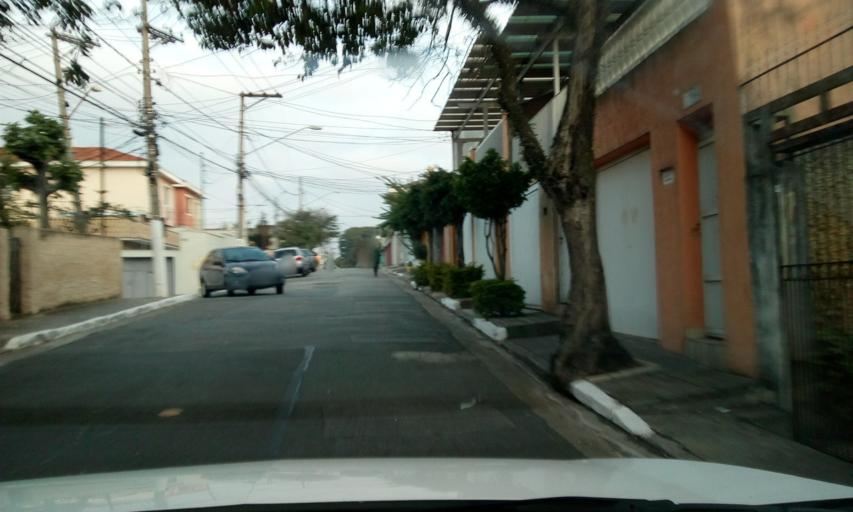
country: BR
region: Sao Paulo
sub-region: Sao Paulo
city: Sao Paulo
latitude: -23.6180
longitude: -46.6448
